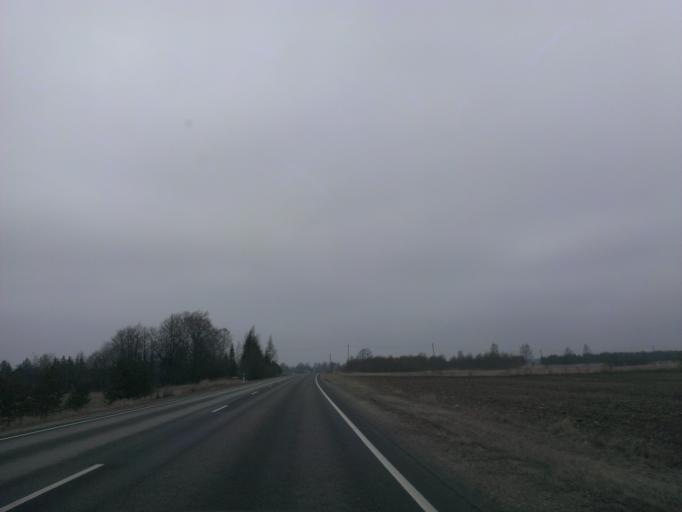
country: EE
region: Paernumaa
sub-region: Audru vald
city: Audru
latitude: 58.4255
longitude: 24.2932
